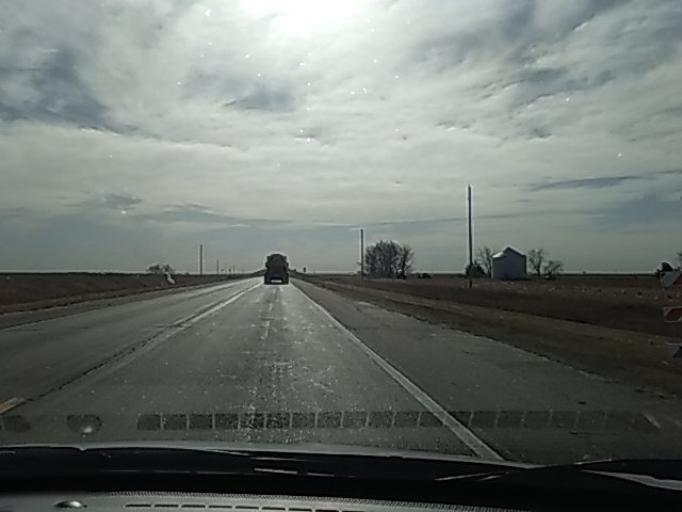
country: US
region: Nebraska
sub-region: Clay County
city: Clay Center
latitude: 40.4105
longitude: -98.0516
